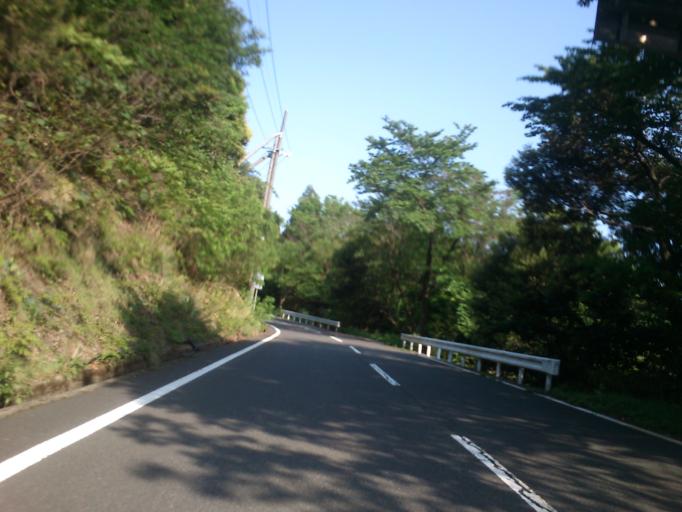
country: JP
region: Kyoto
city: Miyazu
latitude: 35.7499
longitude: 135.1676
